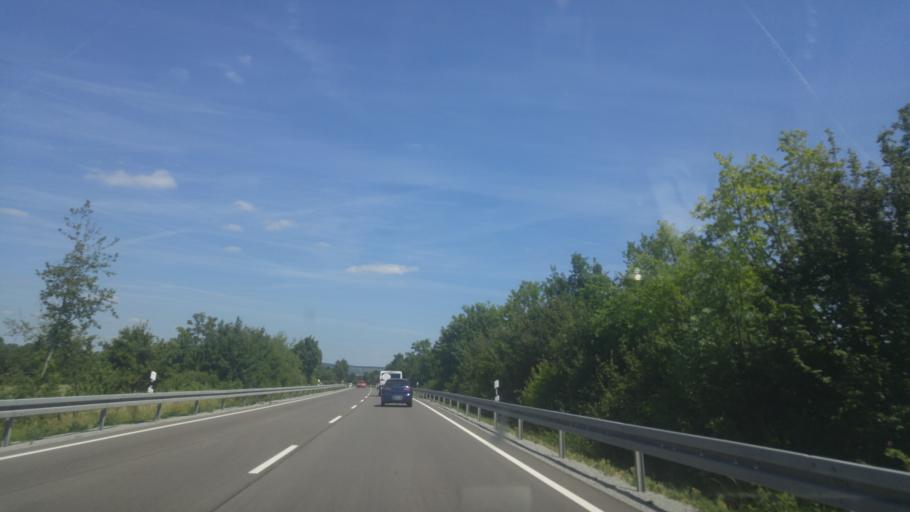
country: DE
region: Bavaria
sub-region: Regierungsbezirk Mittelfranken
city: Bad Windsheim
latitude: 49.4916
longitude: 10.4205
